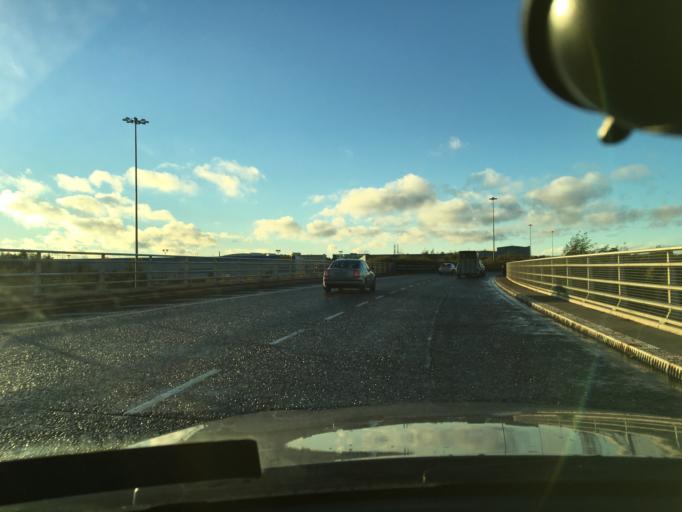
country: IE
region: Leinster
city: Kinsealy-Drinan
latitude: 53.4264
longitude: -6.2173
